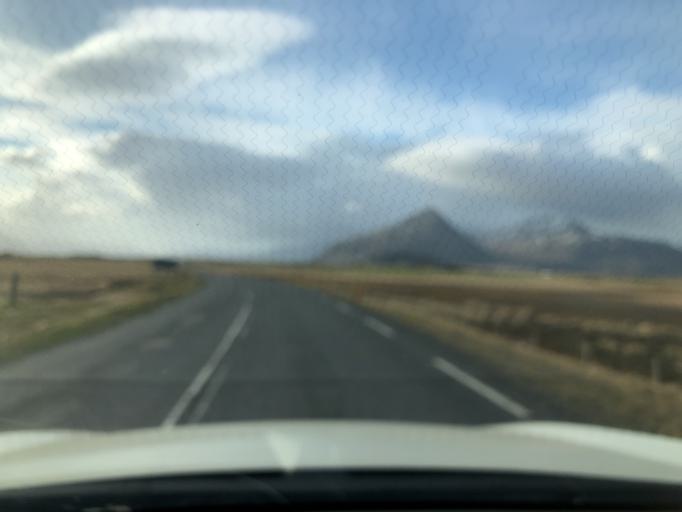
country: IS
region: East
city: Hoefn
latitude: 64.2910
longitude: -15.1829
